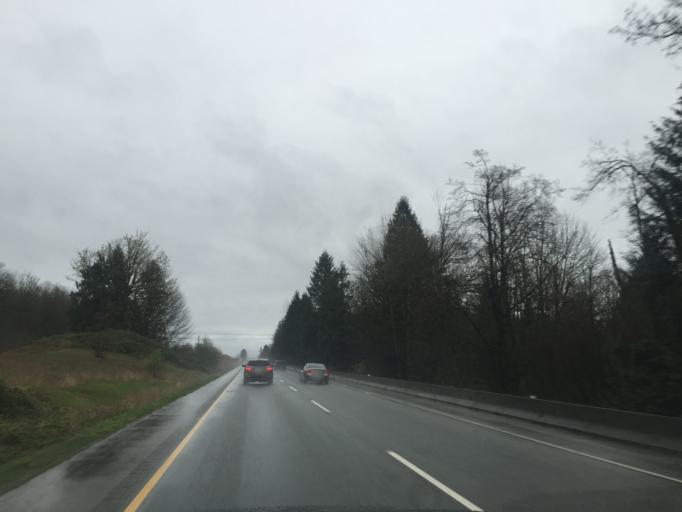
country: CA
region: British Columbia
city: Aldergrove
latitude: 49.0725
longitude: -122.4193
